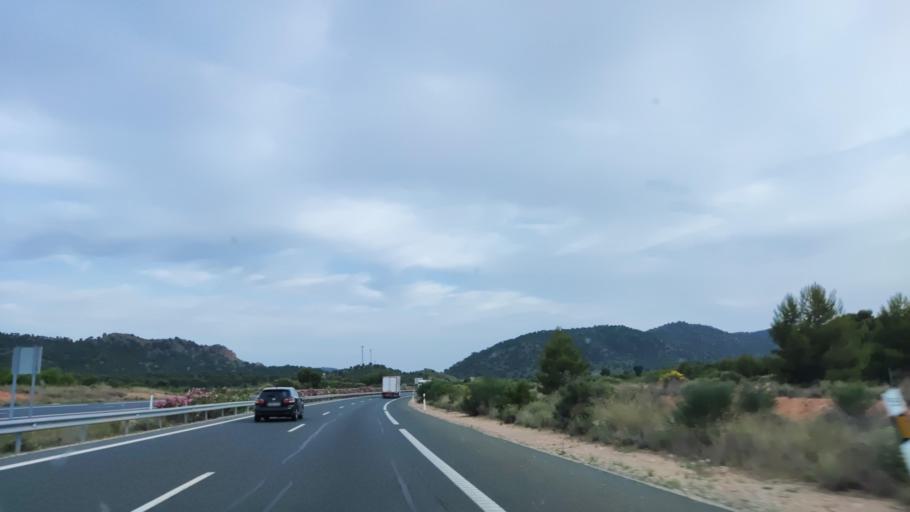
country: ES
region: Castille-La Mancha
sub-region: Provincia de Albacete
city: Tobarra
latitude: 38.6847
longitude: -1.6706
